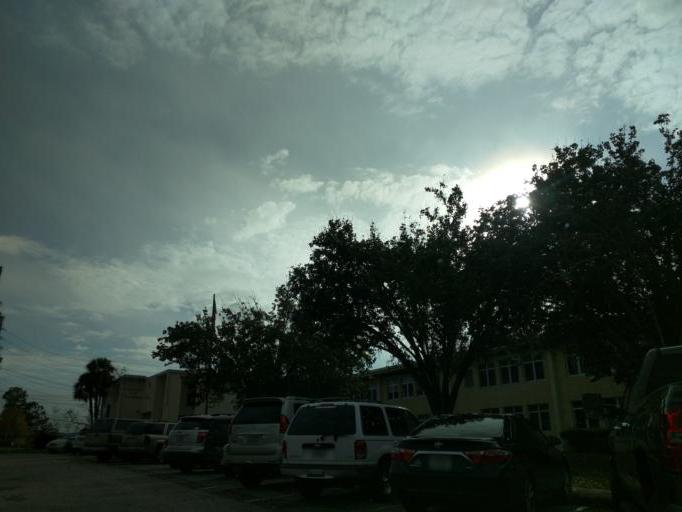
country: US
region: Florida
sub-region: Leon County
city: Tallahassee
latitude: 30.4635
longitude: -84.2866
